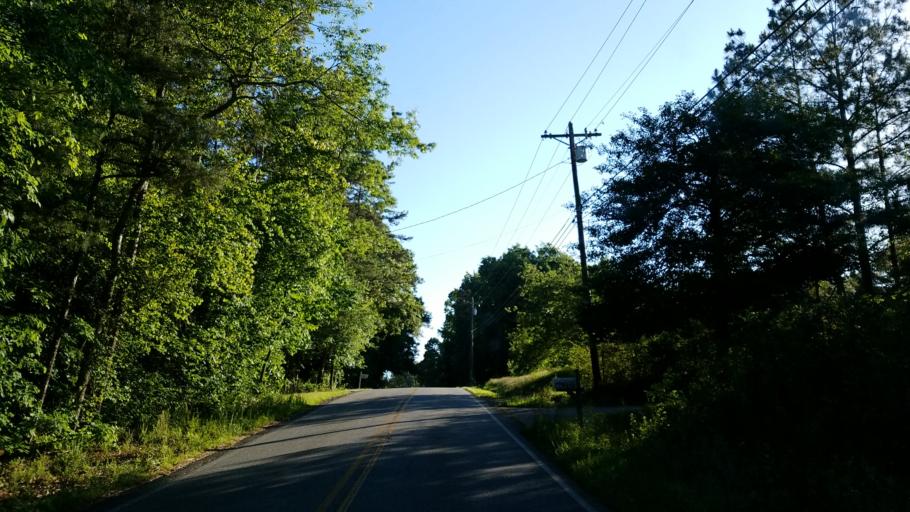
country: US
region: Georgia
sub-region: Cherokee County
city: Holly Springs
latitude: 34.1786
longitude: -84.5384
